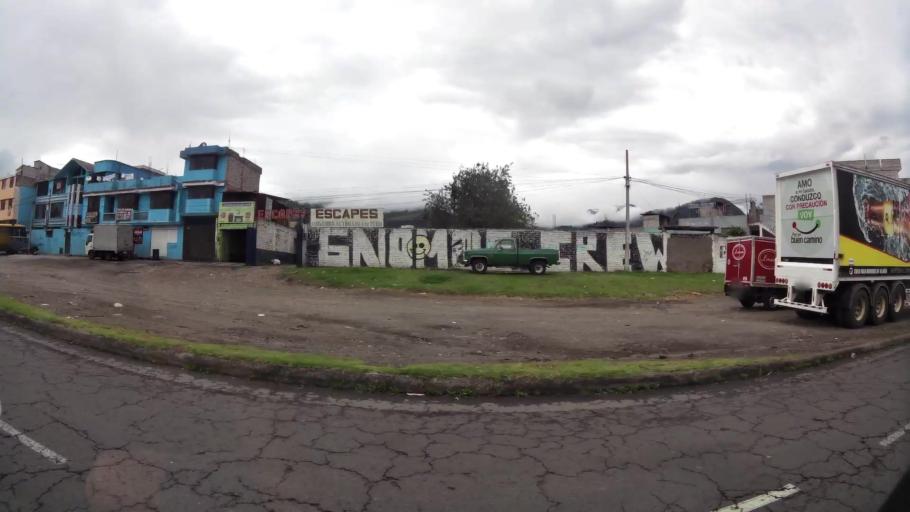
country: EC
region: Pichincha
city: Quito
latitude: -0.2768
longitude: -78.5463
